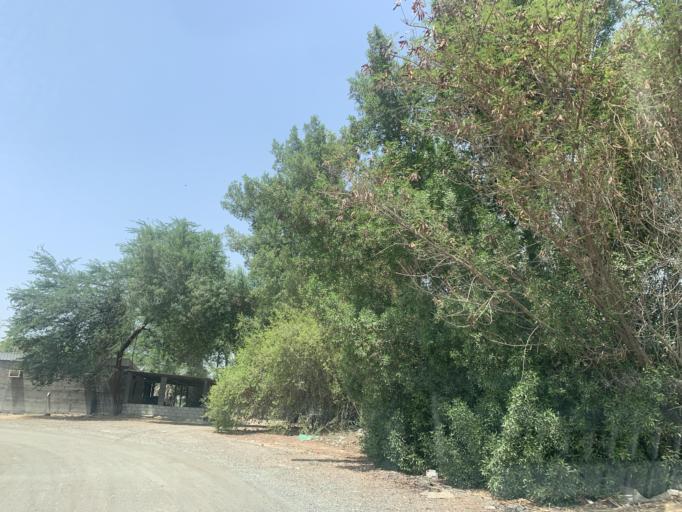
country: BH
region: Central Governorate
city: Madinat Hamad
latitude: 26.1558
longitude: 50.4932
